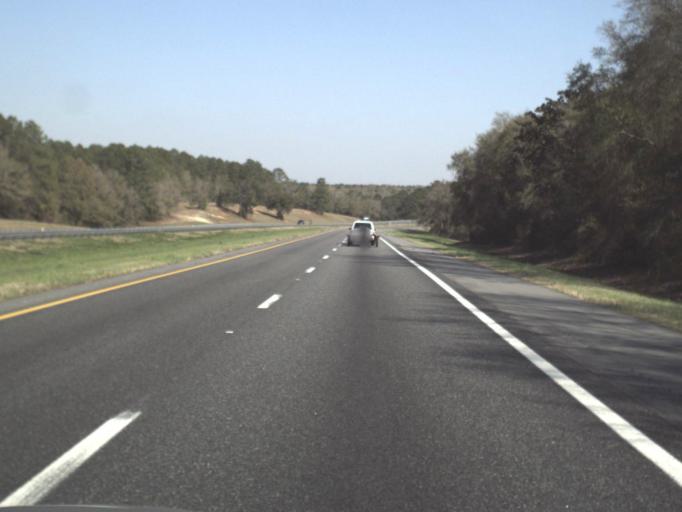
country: US
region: Florida
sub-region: Gadsden County
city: Gretna
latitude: 30.6107
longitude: -84.7512
